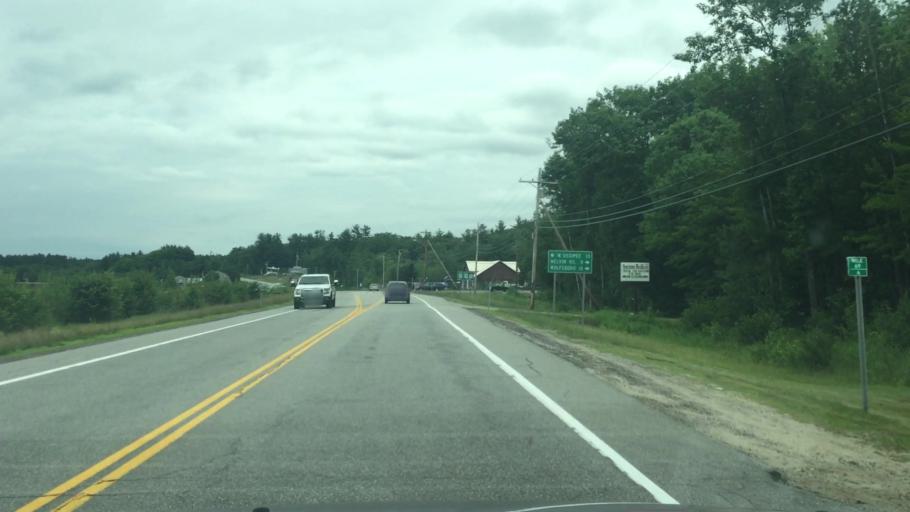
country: US
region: New Hampshire
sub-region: Carroll County
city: Moultonborough
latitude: 43.7602
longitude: -71.3893
